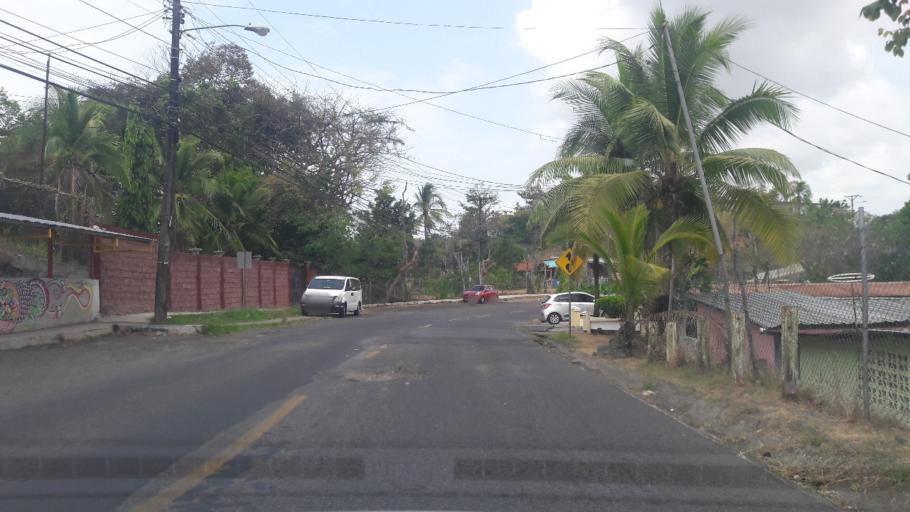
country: PA
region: Panama
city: Alcalde Diaz
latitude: 9.1134
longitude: -79.5557
